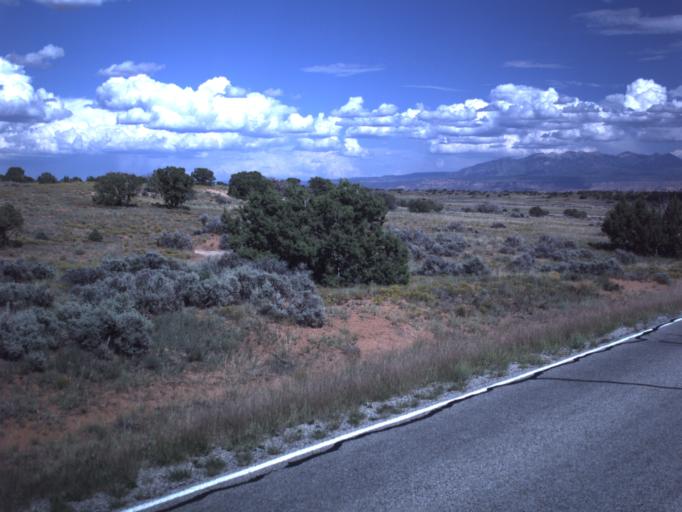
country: US
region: Utah
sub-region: Grand County
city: Moab
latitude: 38.5226
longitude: -109.7405
